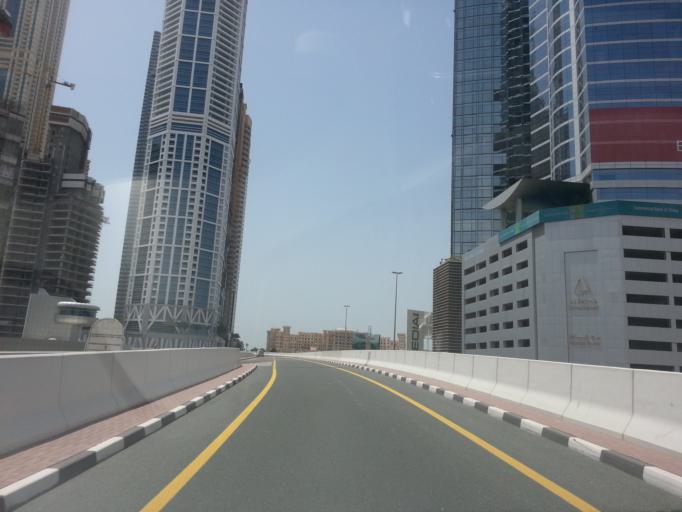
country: AE
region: Dubai
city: Dubai
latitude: 25.0884
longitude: 55.1532
